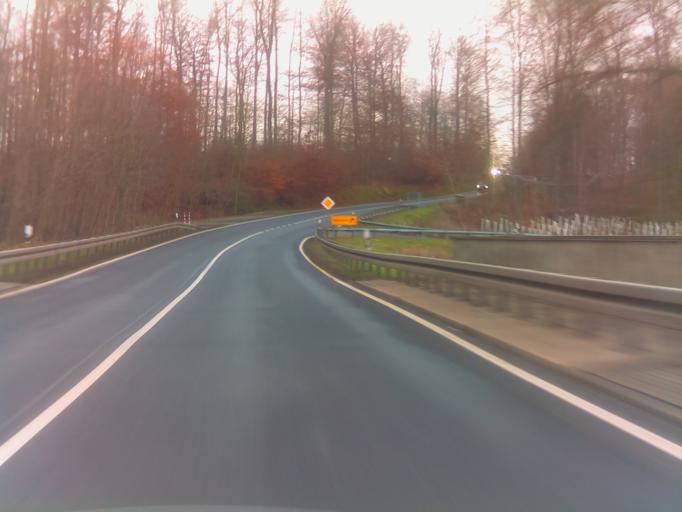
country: DE
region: Thuringia
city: Unterbreizbach
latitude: 50.7839
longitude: 9.9883
